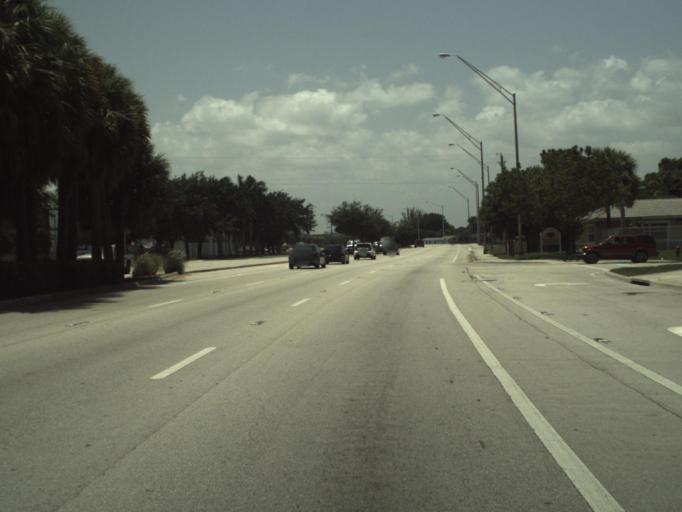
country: US
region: Florida
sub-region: Broward County
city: Pompano Beach
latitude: 26.2371
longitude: -80.1532
